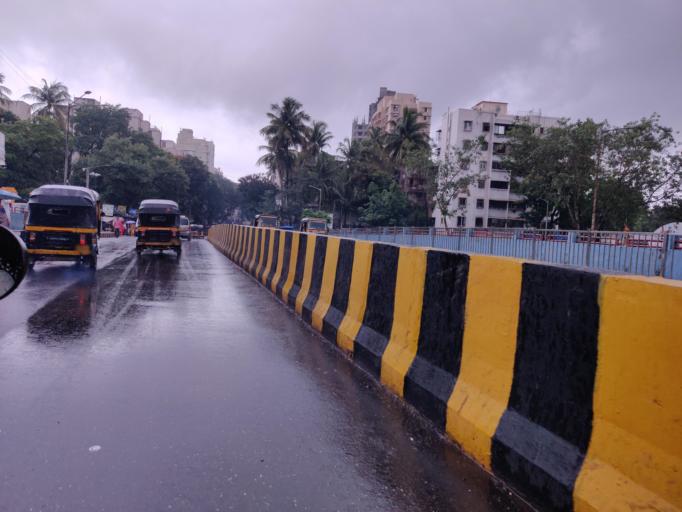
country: IN
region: Maharashtra
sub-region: Mumbai Suburban
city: Borivli
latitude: 19.2552
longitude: 72.8568
